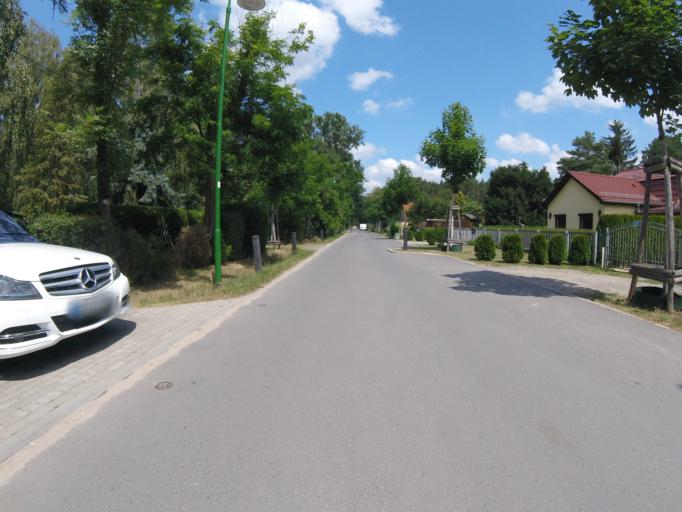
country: DE
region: Brandenburg
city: Bestensee
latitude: 52.2630
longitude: 13.6566
